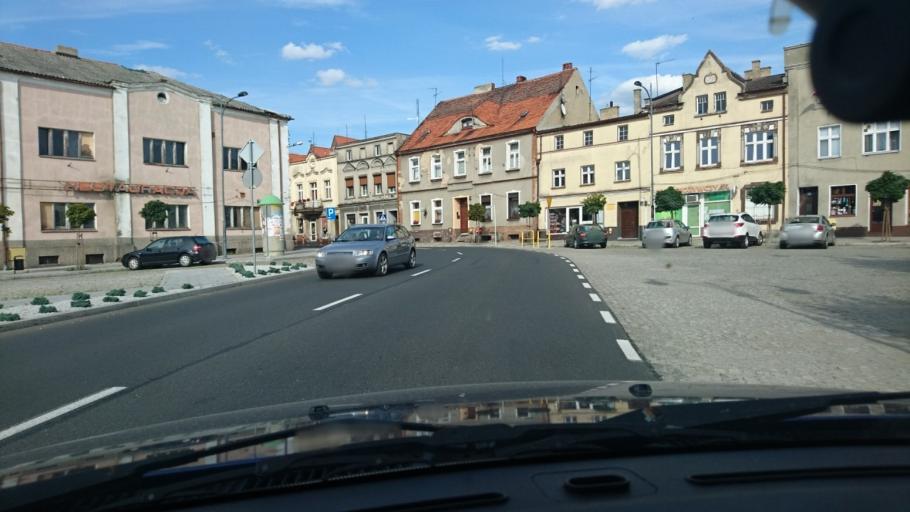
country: PL
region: Greater Poland Voivodeship
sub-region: Powiat krotoszynski
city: Kobylin
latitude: 51.7138
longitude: 17.2259
